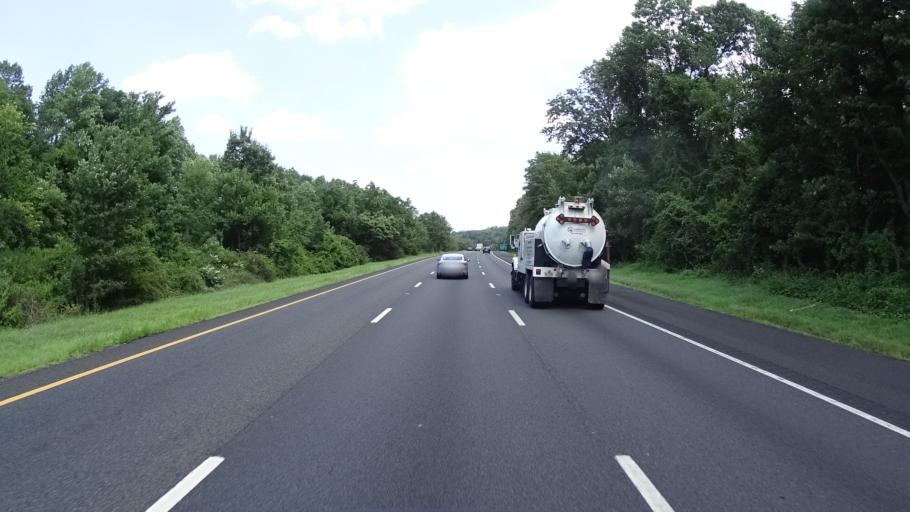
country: US
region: New Jersey
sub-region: Somerset County
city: Watchung
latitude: 40.6511
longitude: -74.4649
